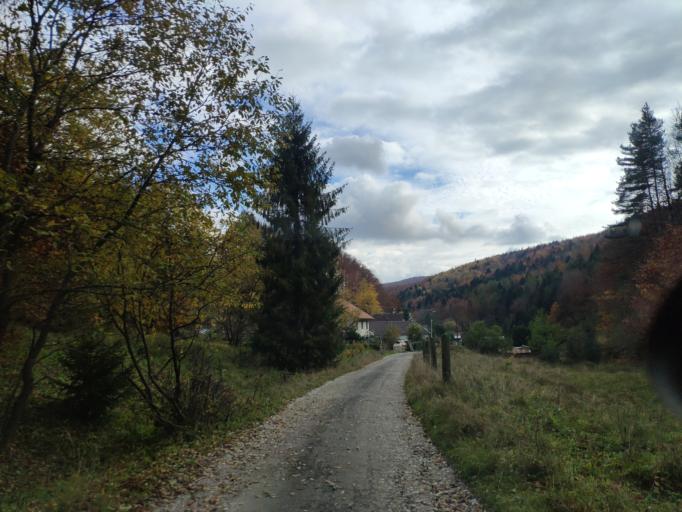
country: SK
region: Kosicky
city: Gelnica
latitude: 48.7590
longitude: 20.9867
